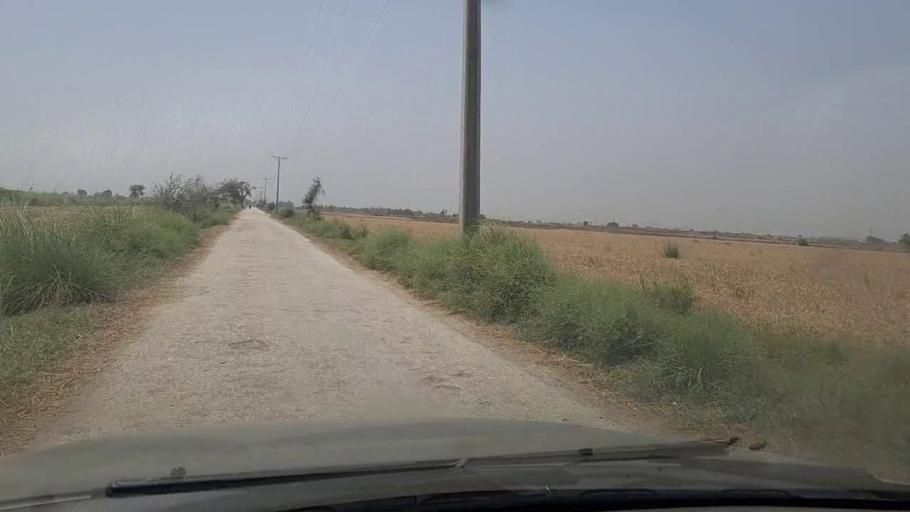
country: PK
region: Sindh
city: Miro Khan
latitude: 27.7642
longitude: 68.1318
